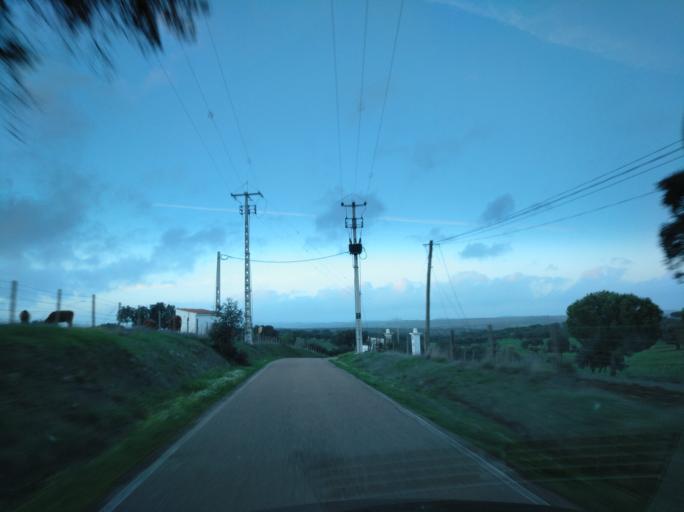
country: PT
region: Portalegre
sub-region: Campo Maior
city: Campo Maior
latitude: 39.0752
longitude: -7.1157
